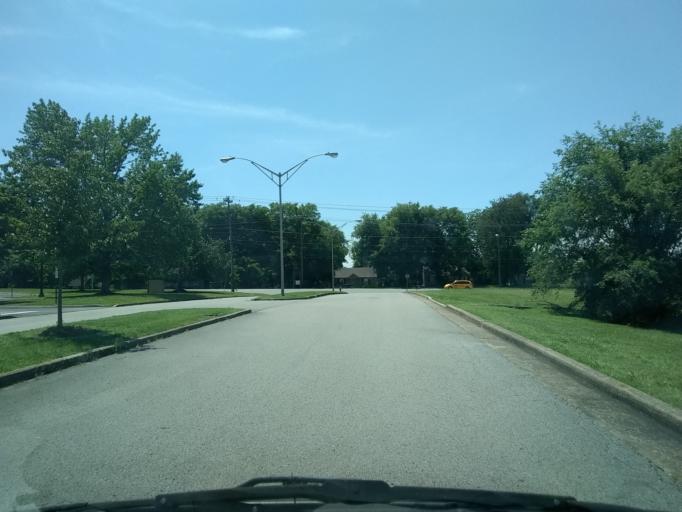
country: US
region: Tennessee
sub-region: Davidson County
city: Oak Hill
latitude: 36.1270
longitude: -86.6947
